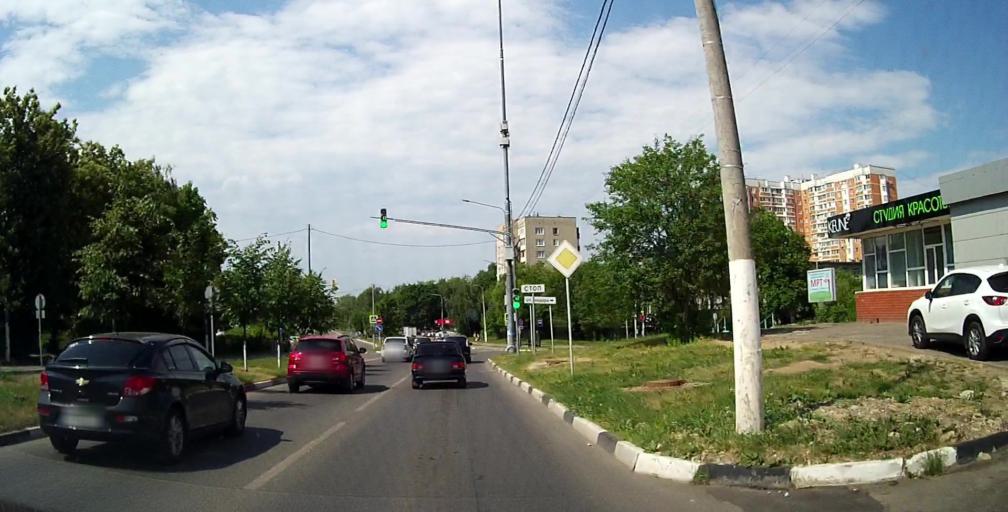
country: RU
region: Moskovskaya
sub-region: Podol'skiy Rayon
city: Podol'sk
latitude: 55.4181
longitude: 37.5200
